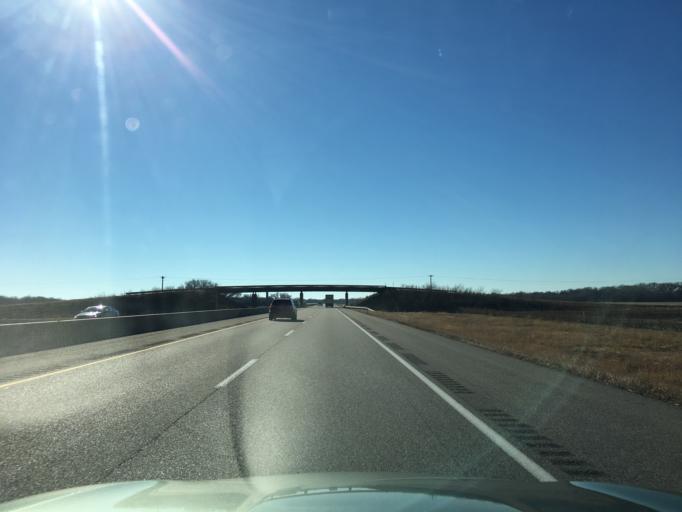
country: US
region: Kansas
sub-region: Sumner County
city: Belle Plaine
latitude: 37.4084
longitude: -97.3233
